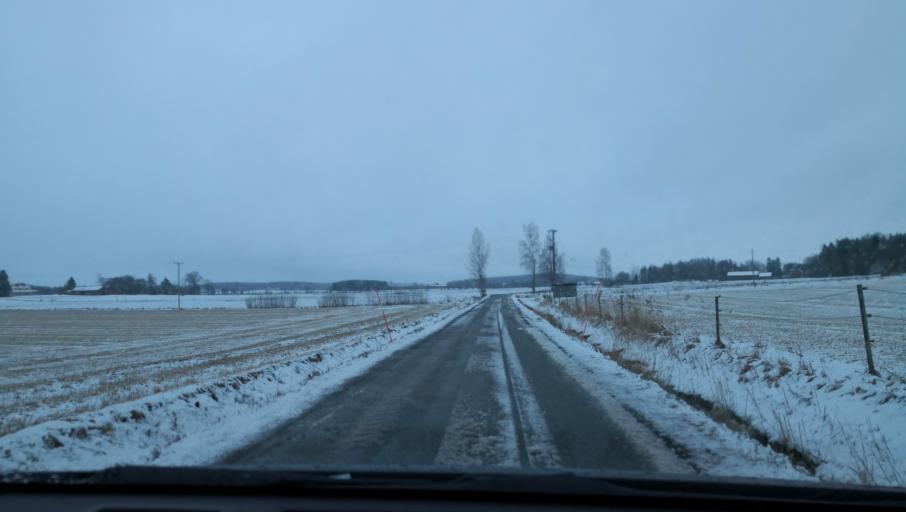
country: SE
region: Vaestmanland
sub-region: Kopings Kommun
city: Kolsva
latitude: 59.5568
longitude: 15.8714
